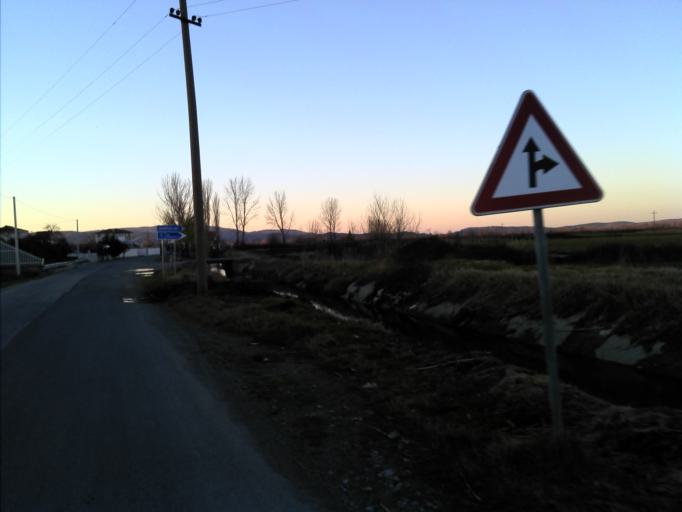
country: AL
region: Shkoder
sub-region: Rrethi i Shkodres
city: Berdica e Madhe
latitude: 42.0095
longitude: 19.4807
